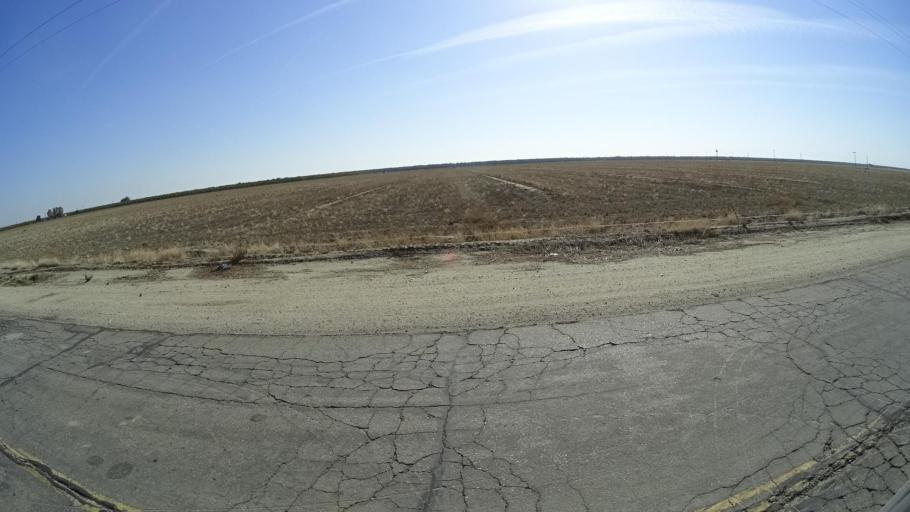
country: US
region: California
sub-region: Kern County
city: Wasco
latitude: 35.6670
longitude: -119.3810
